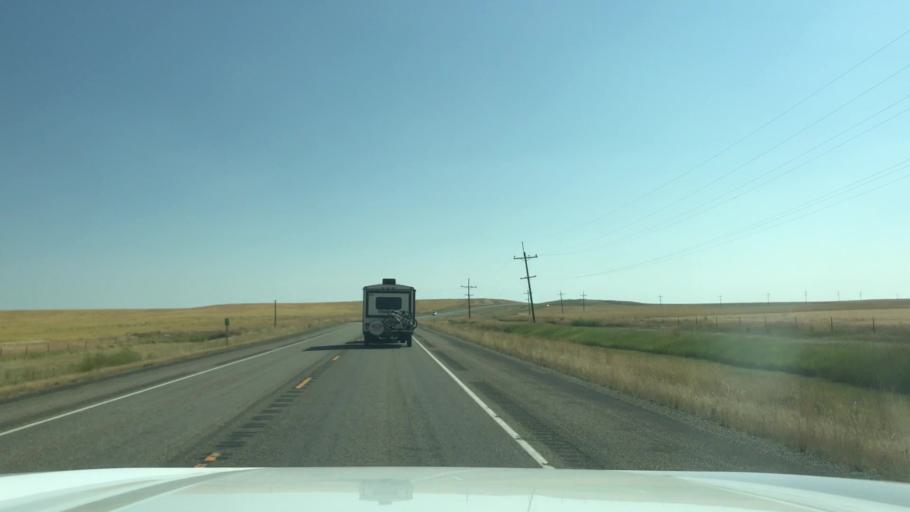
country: US
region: Montana
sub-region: Wheatland County
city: Harlowton
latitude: 46.4761
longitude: -109.7661
